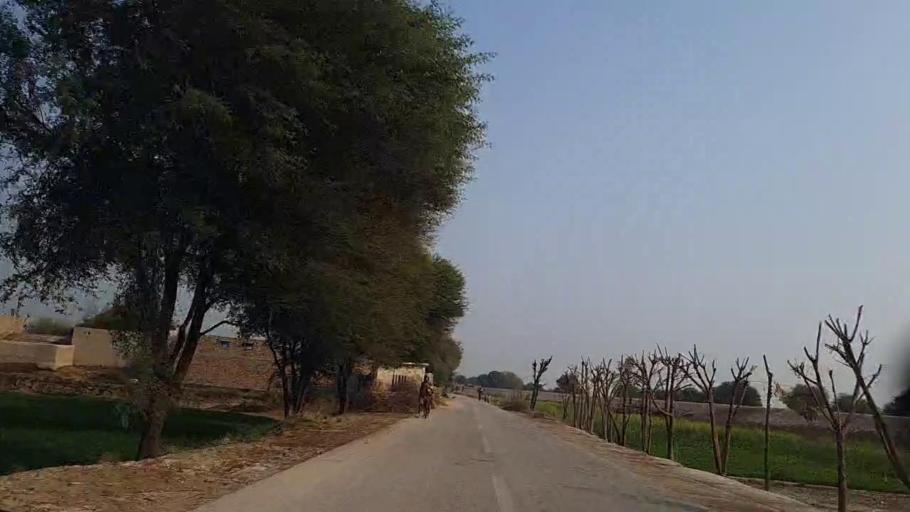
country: PK
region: Sindh
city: Sann
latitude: 26.1507
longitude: 68.1260
